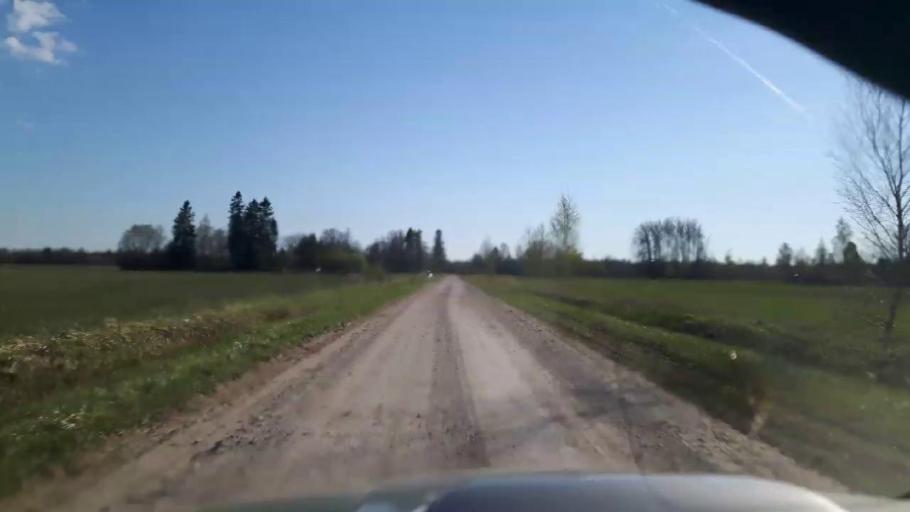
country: EE
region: Paernumaa
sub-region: Tootsi vald
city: Tootsi
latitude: 58.4429
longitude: 24.8560
